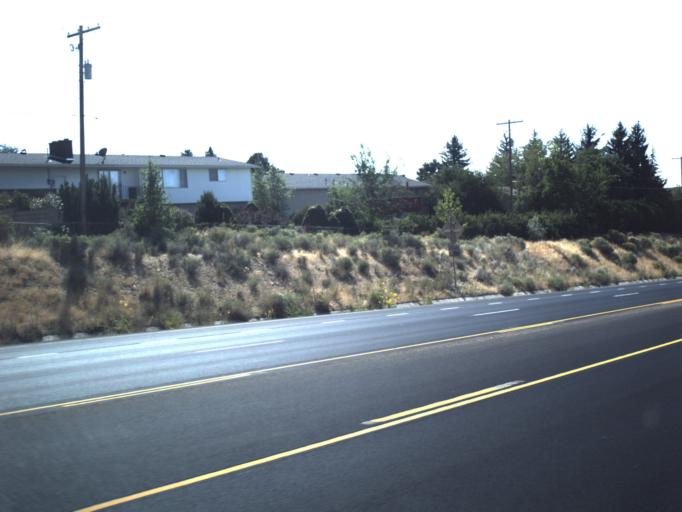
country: US
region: Utah
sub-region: Box Elder County
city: Brigham City
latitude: 41.4866
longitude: -112.0129
